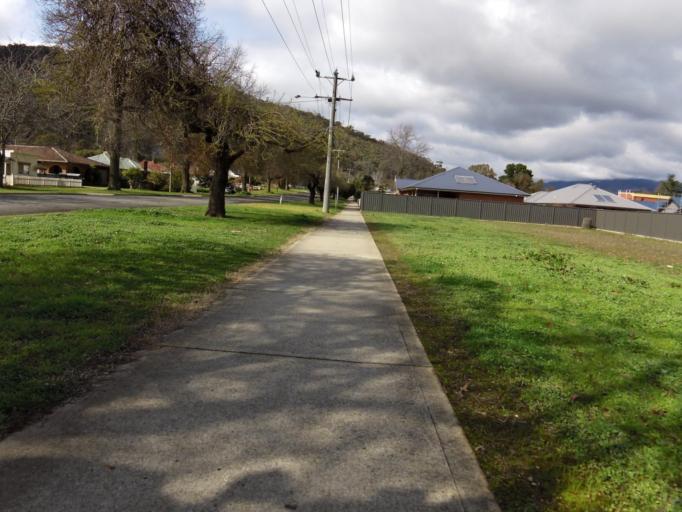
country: AU
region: Victoria
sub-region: Wangaratta
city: Wangaratta
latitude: -36.5626
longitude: 146.7286
